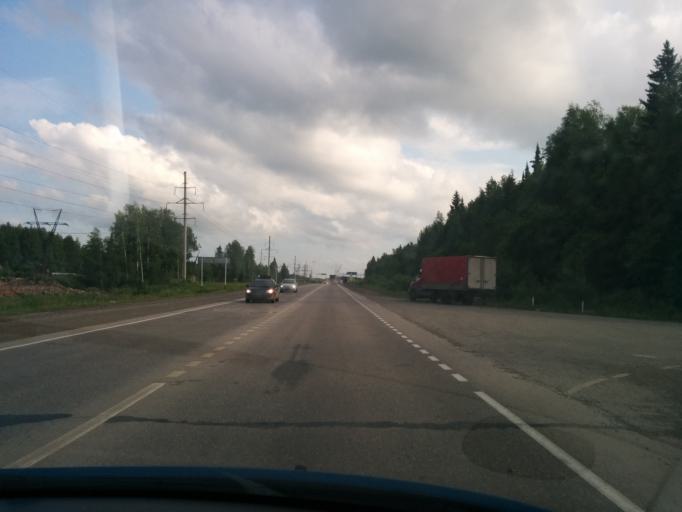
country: RU
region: Perm
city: Novyye Lyady
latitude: 58.0567
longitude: 56.4279
